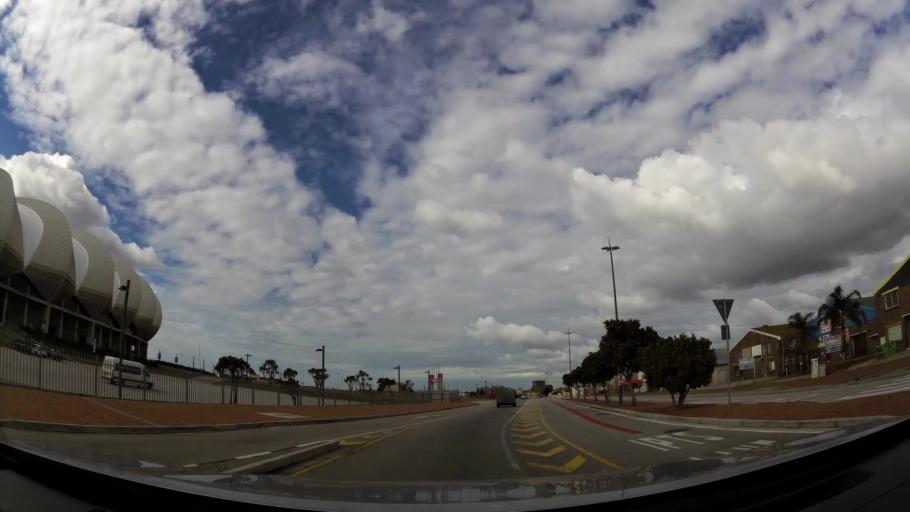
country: ZA
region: Eastern Cape
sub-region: Nelson Mandela Bay Metropolitan Municipality
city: Port Elizabeth
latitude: -33.9392
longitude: 25.5978
